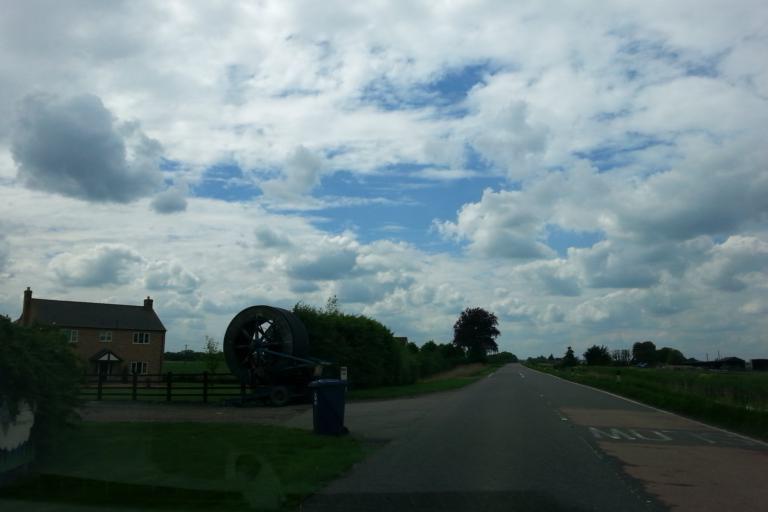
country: GB
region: England
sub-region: Cambridgeshire
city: Ramsey
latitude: 52.4677
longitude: -0.1320
